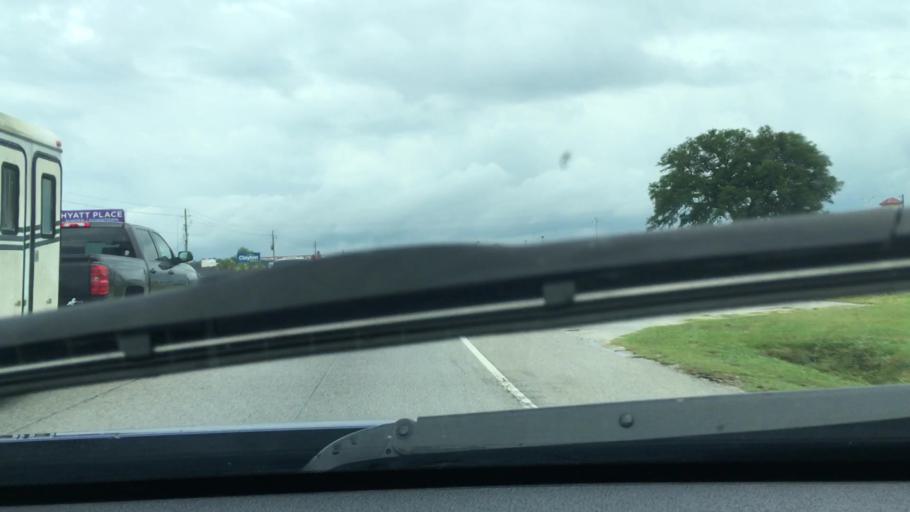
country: US
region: South Carolina
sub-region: Sumter County
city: Cherryvale
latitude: 33.9644
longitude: -80.4051
